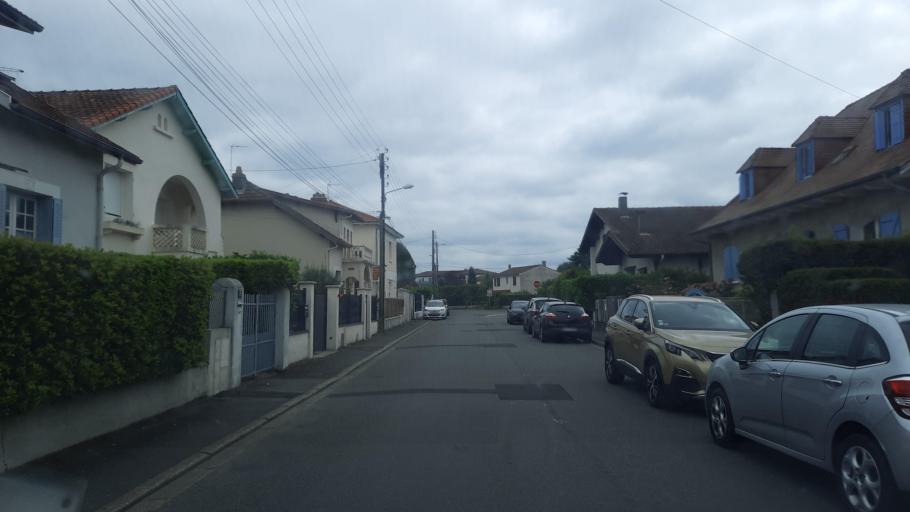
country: FR
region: Midi-Pyrenees
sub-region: Departement des Hautes-Pyrenees
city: Laloubere
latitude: 43.2198
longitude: 0.0619
